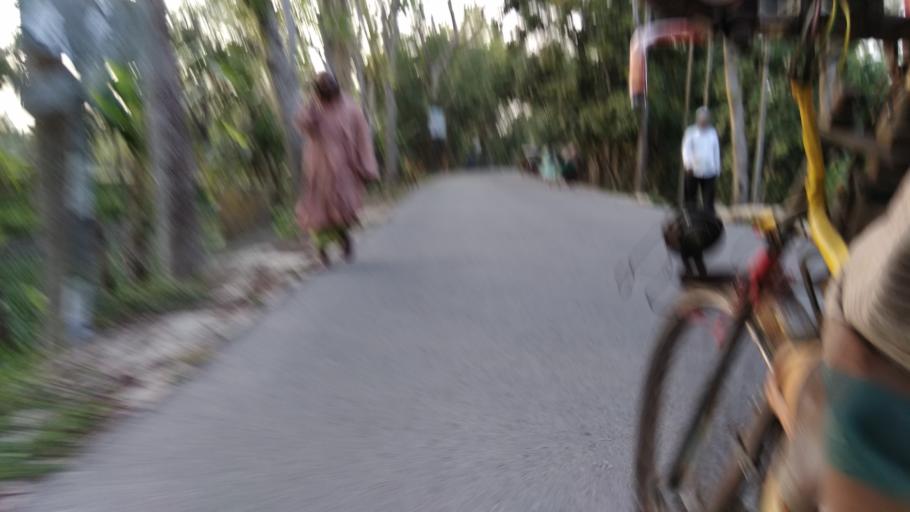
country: BD
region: Barisal
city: Mehendiganj
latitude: 22.9229
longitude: 90.4064
